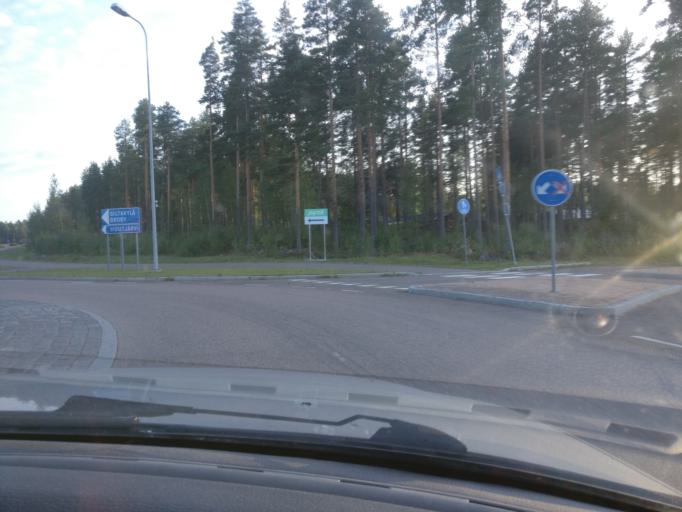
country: FI
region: Kymenlaakso
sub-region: Kotka-Hamina
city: Broby
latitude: 60.5016
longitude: 26.7412
